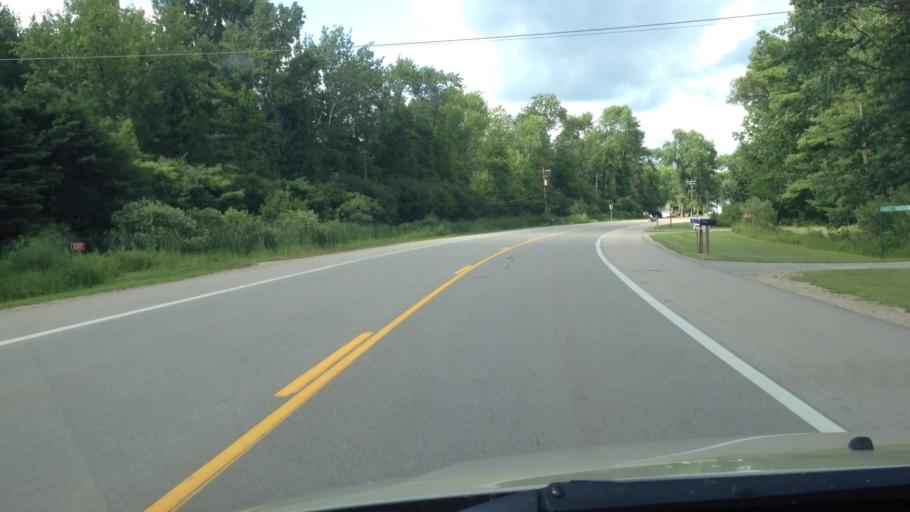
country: US
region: Michigan
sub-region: Menominee County
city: Menominee
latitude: 45.1483
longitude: -87.6029
